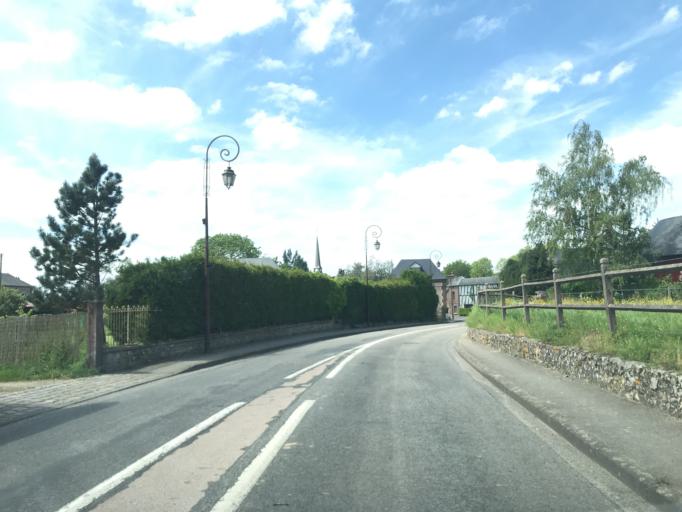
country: FR
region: Haute-Normandie
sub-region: Departement de l'Eure
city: Nassandres
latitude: 49.1652
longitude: 0.7884
